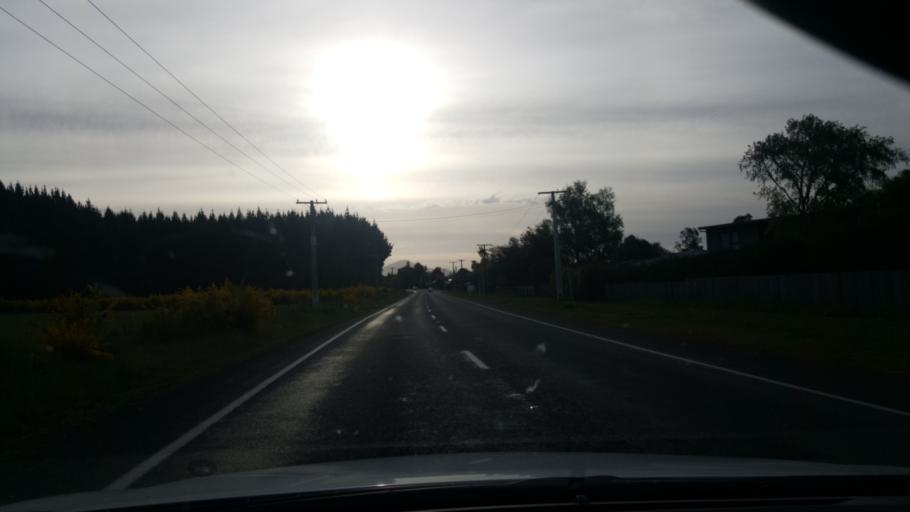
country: NZ
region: Waikato
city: Turangi
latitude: -38.9071
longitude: 175.9223
